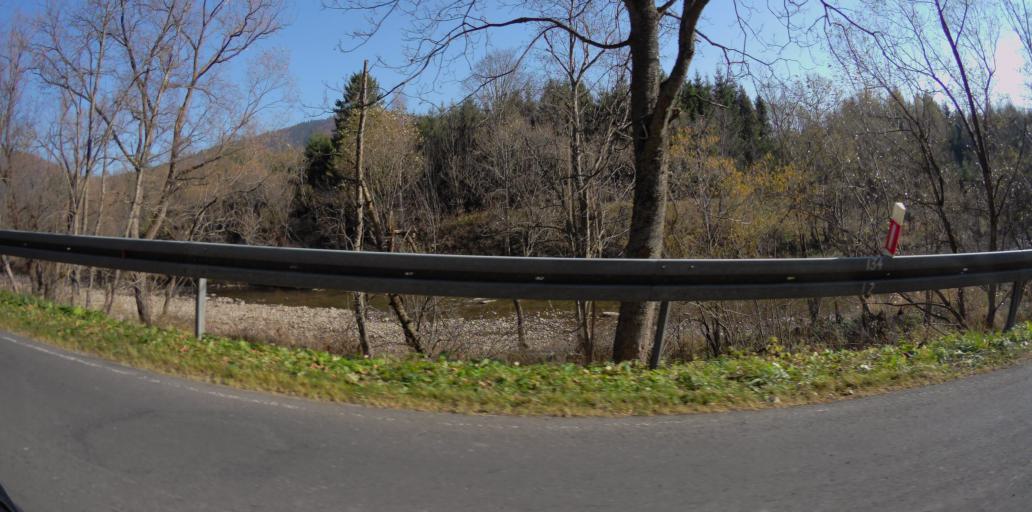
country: PL
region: Subcarpathian Voivodeship
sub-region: Powiat bieszczadzki
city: Lutowiska
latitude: 49.1832
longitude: 22.6820
